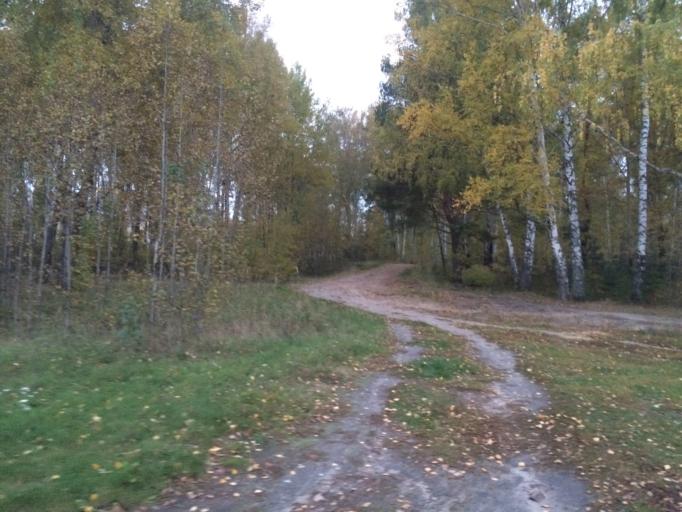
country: RU
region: Nizjnij Novgorod
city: Sarov
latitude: 54.9416
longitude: 43.3414
